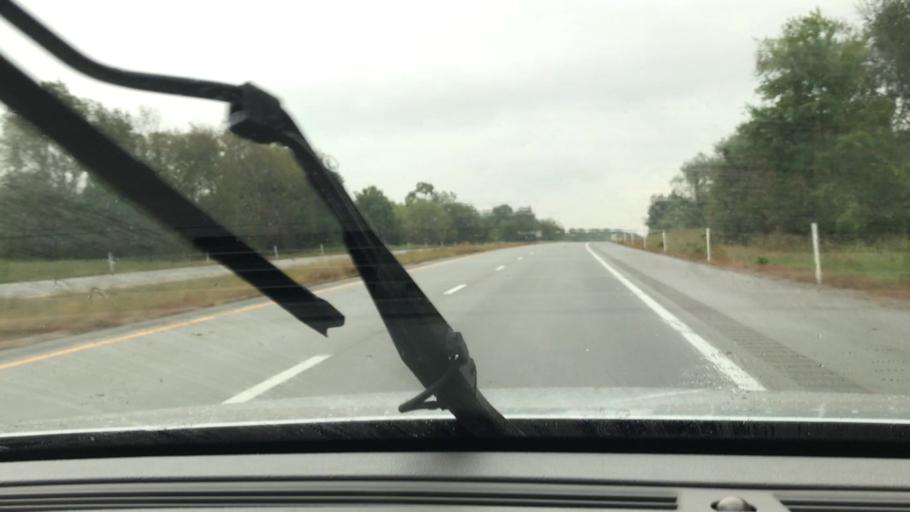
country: US
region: Kentucky
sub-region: Barren County
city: Glasgow
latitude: 37.0079
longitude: -86.0117
